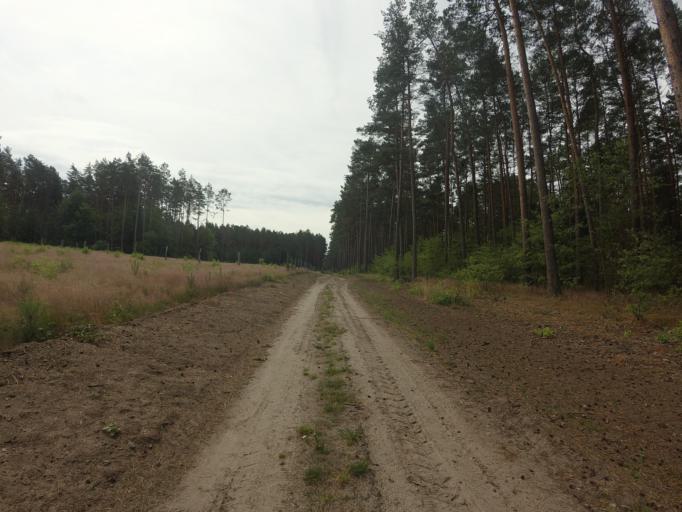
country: PL
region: West Pomeranian Voivodeship
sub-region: Powiat choszczenski
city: Bierzwnik
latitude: 53.1340
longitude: 15.6842
